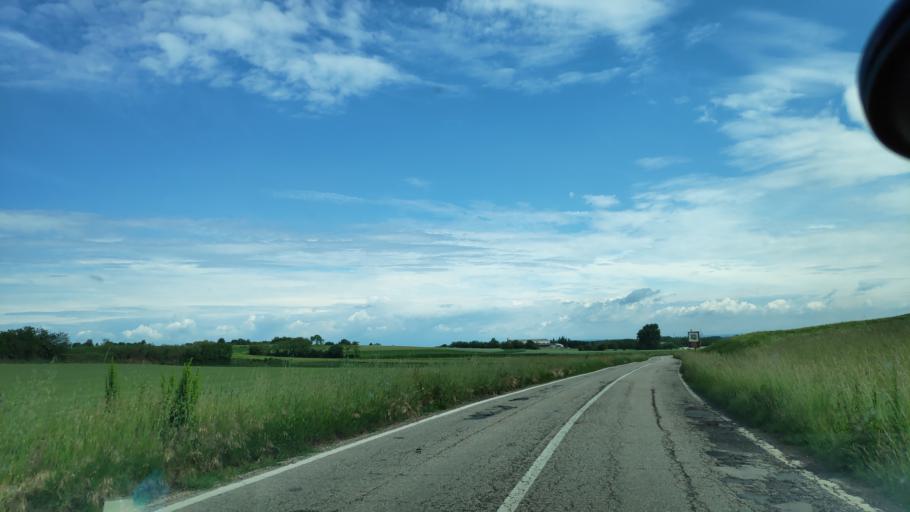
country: IT
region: Piedmont
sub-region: Provincia di Torino
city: Cambiano
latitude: 44.9902
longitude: 7.7777
